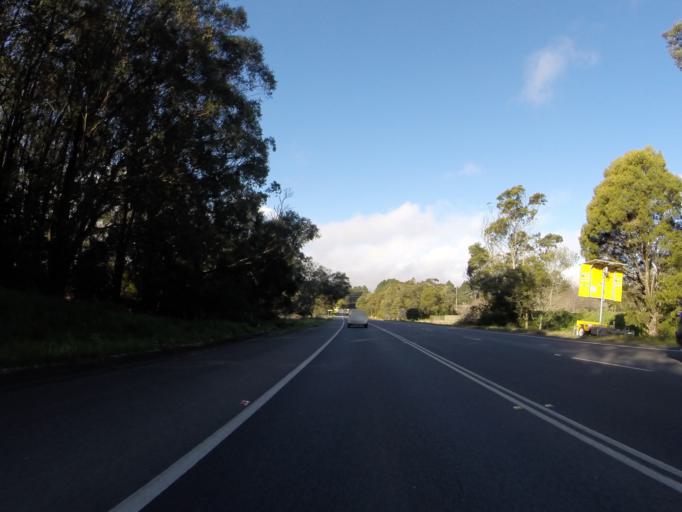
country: AU
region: New South Wales
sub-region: Shellharbour
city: Calderwood
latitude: -34.5891
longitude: 150.5761
